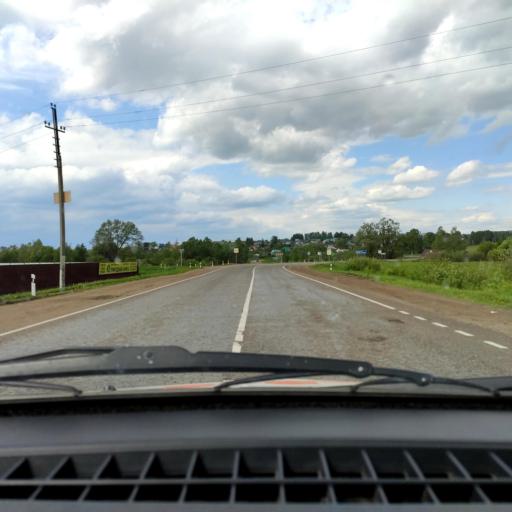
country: RU
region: Bashkortostan
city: Iglino
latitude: 54.9090
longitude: 56.4751
